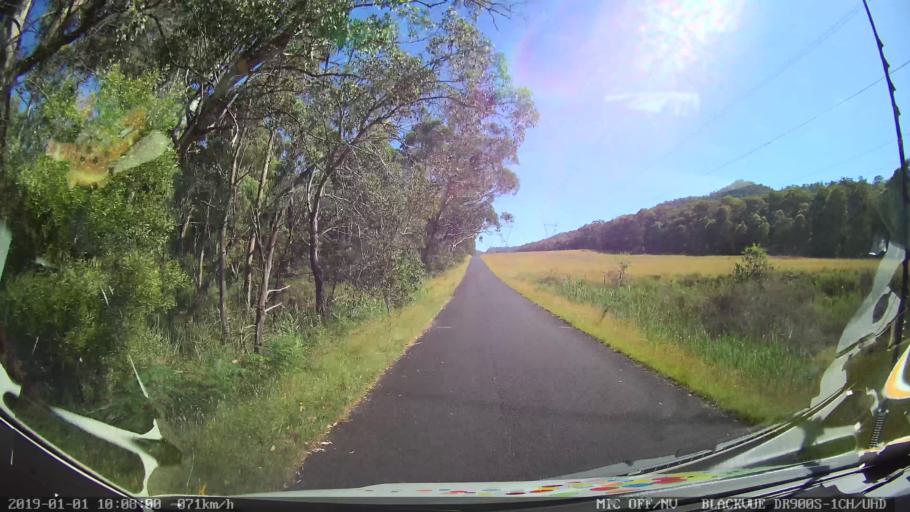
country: AU
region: New South Wales
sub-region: Snowy River
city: Jindabyne
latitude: -36.1638
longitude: 148.1572
